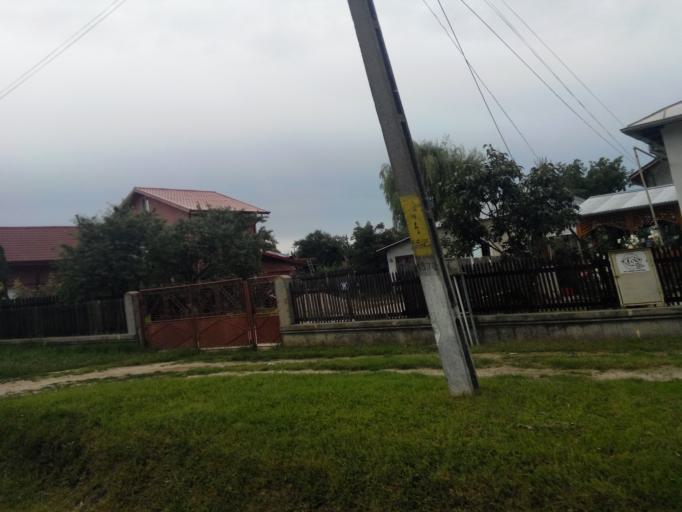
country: RO
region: Arges
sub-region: Comuna Bascov
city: Bascov
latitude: 44.9126
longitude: 24.8048
